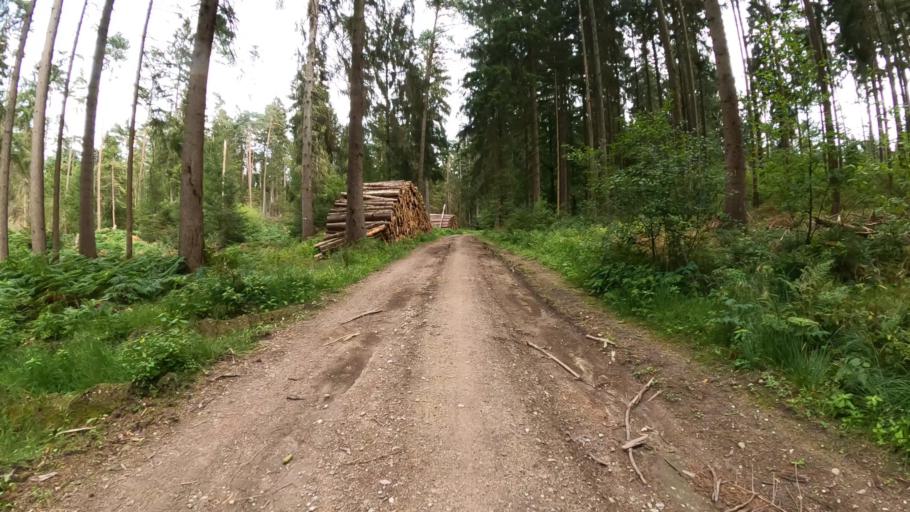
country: DE
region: Lower Saxony
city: Seevetal
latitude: 53.3833
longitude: 9.9311
